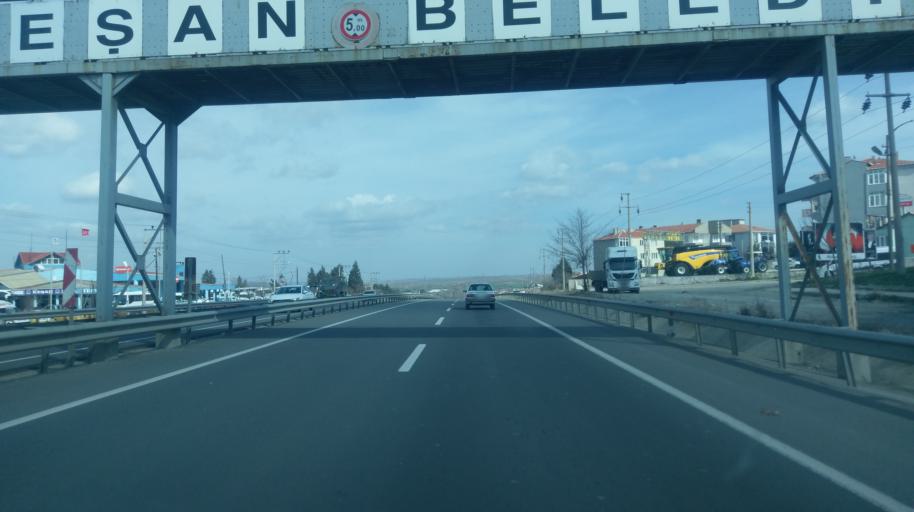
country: TR
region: Edirne
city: Kesan
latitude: 40.8661
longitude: 26.6248
